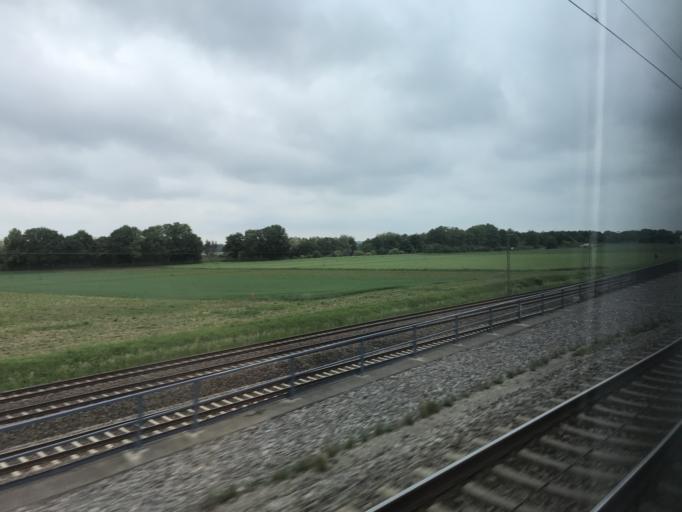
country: DE
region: Bavaria
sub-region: Upper Bavaria
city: Maisach
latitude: 48.2137
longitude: 11.2766
